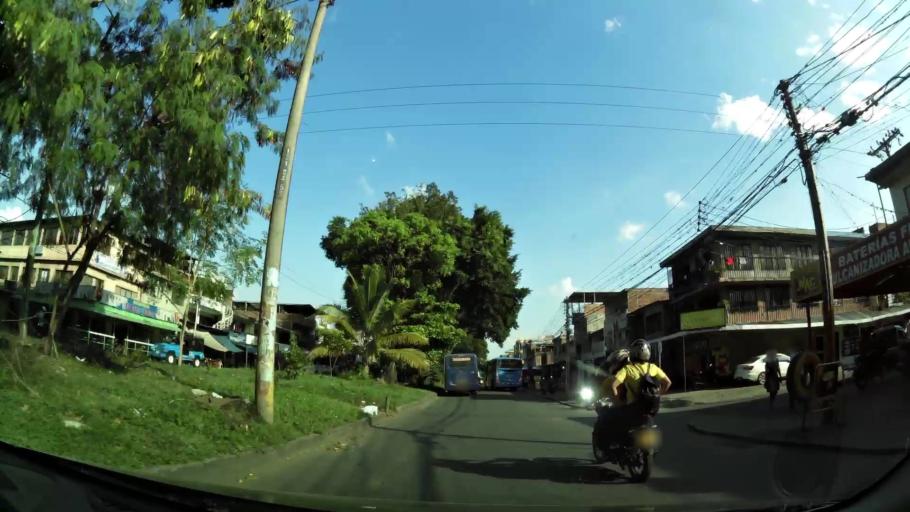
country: CO
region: Valle del Cauca
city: Cali
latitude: 3.4039
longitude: -76.5127
